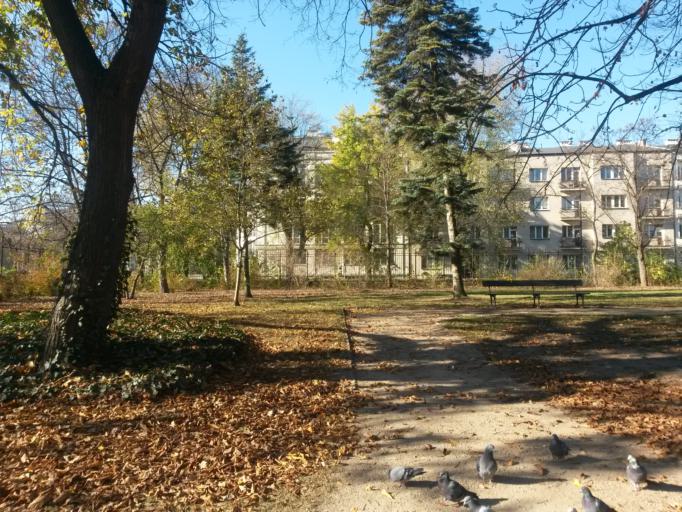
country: PL
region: Masovian Voivodeship
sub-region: Warszawa
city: Mokotow
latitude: 52.2074
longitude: 21.0326
